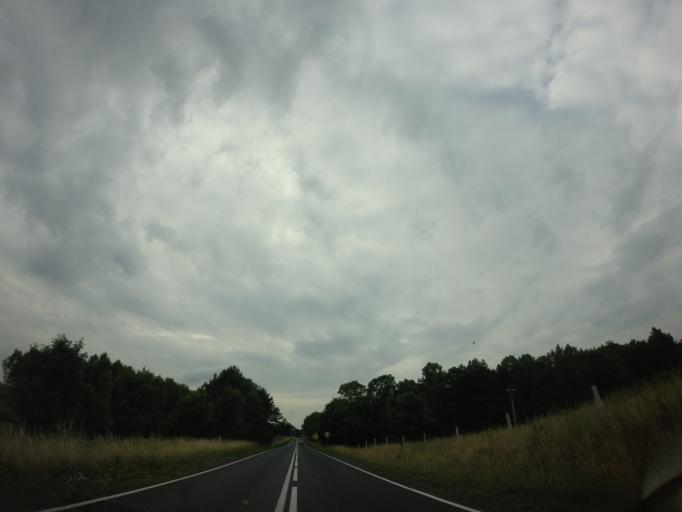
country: PL
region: West Pomeranian Voivodeship
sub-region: Powiat szczecinecki
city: Borne Sulinowo
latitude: 53.6112
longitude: 16.5607
